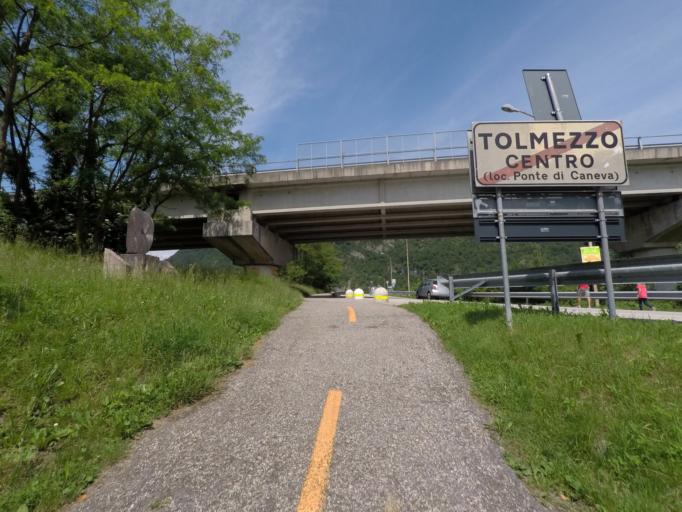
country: IT
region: Friuli Venezia Giulia
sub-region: Provincia di Udine
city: Tolmezzo
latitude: 46.4085
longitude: 13.0081
